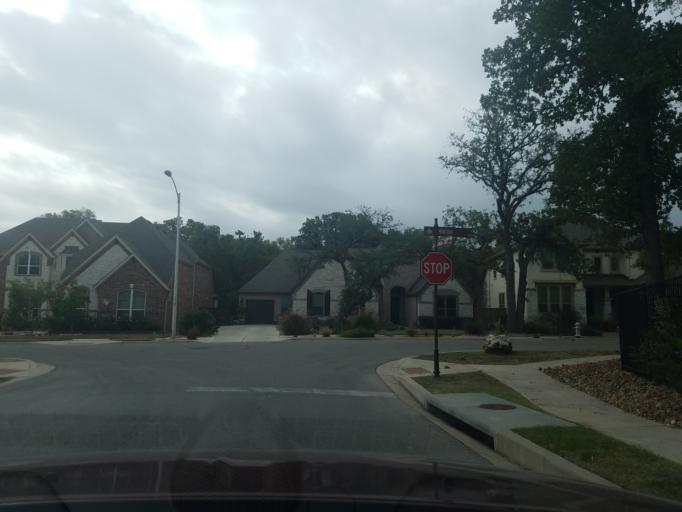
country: US
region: Texas
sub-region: Williamson County
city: Anderson Mill
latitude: 30.4852
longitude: -97.7938
